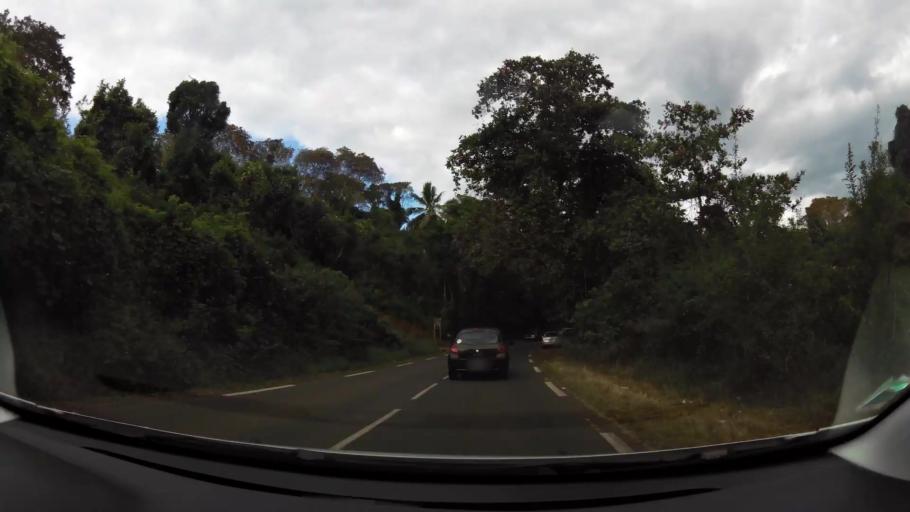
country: YT
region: Dembeni
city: Dembeni
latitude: -12.8414
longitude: 45.1668
